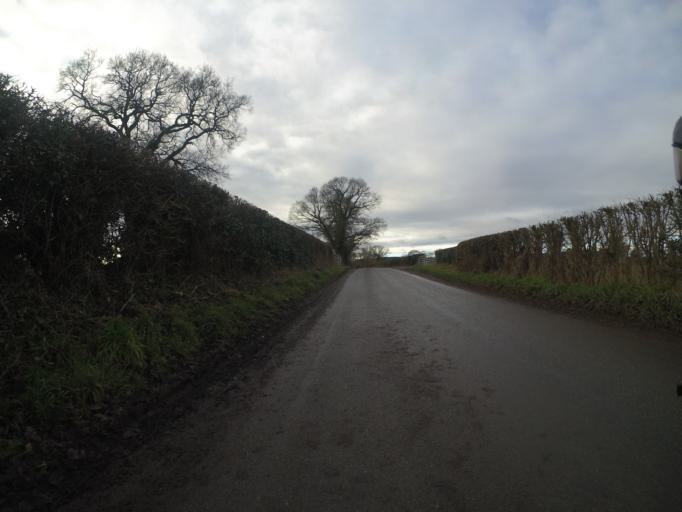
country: GB
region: England
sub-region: Cheshire West and Chester
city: Tiverton
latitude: 53.1201
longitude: -2.6673
